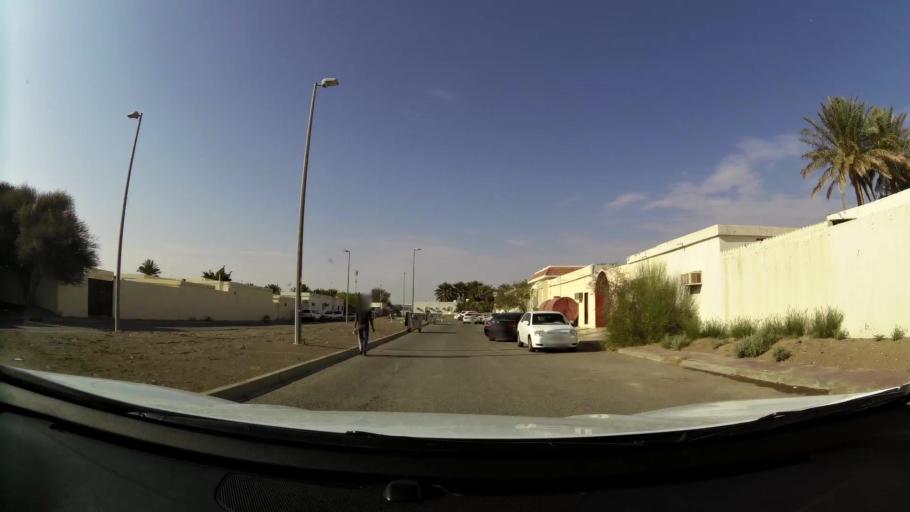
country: AE
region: Abu Dhabi
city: Al Ain
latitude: 24.0431
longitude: 55.8451
